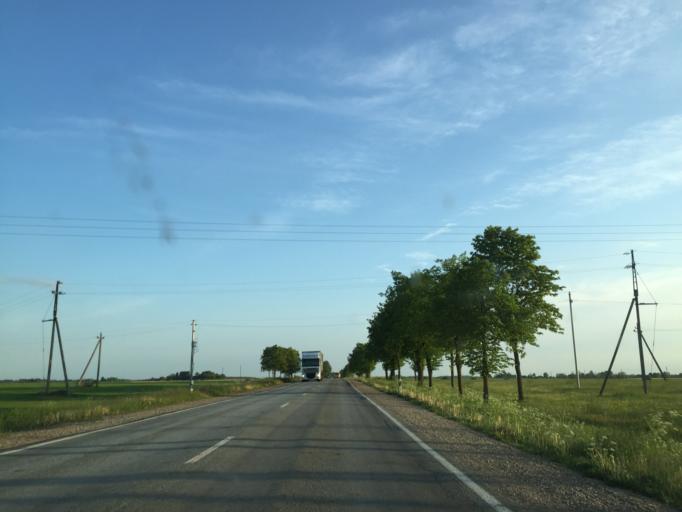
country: LT
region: Siauliu apskritis
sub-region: Siauliai
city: Siauliai
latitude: 56.0721
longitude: 23.4522
